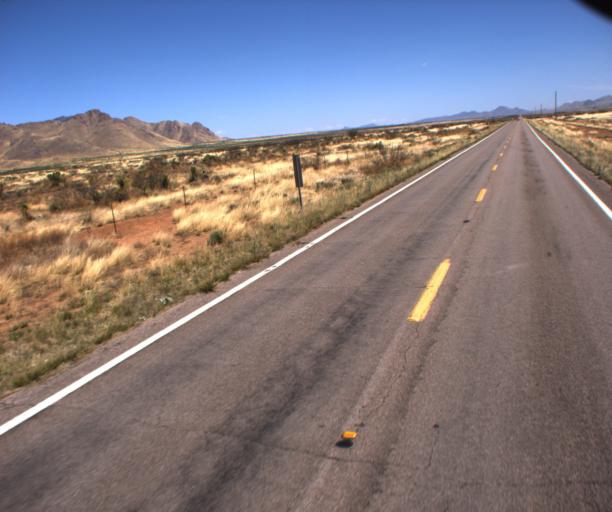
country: US
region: Arizona
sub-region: Cochise County
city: Douglas
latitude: 31.7063
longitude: -109.1219
